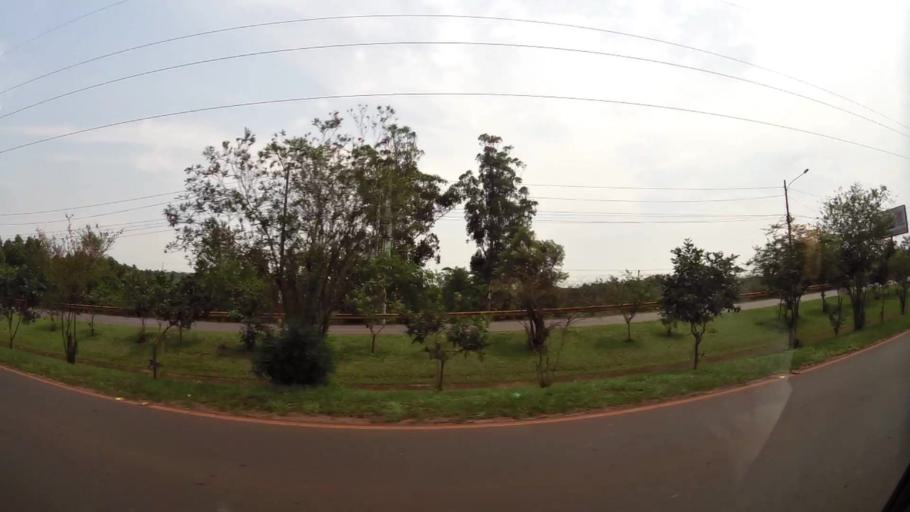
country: PY
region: Alto Parana
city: Ciudad del Este
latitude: -25.4844
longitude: -54.6275
